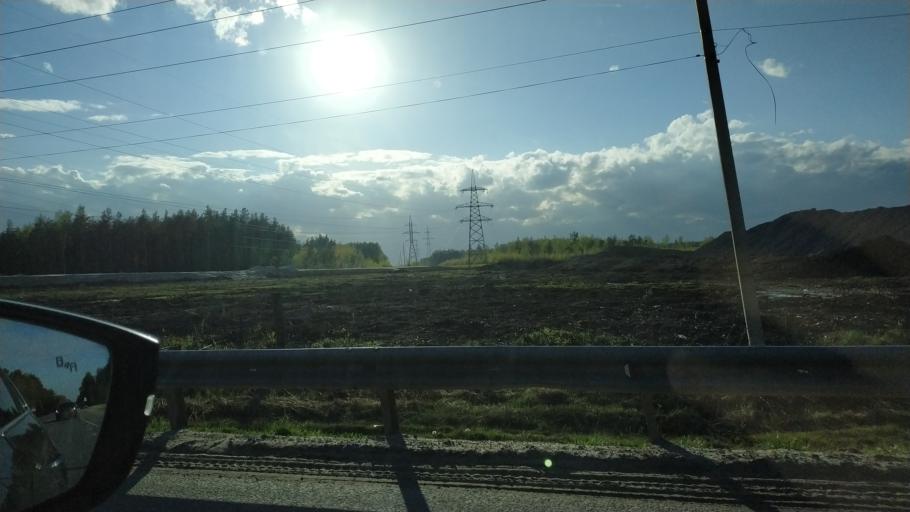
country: RU
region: Moskovskaya
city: Gzhel'
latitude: 55.6361
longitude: 38.3637
